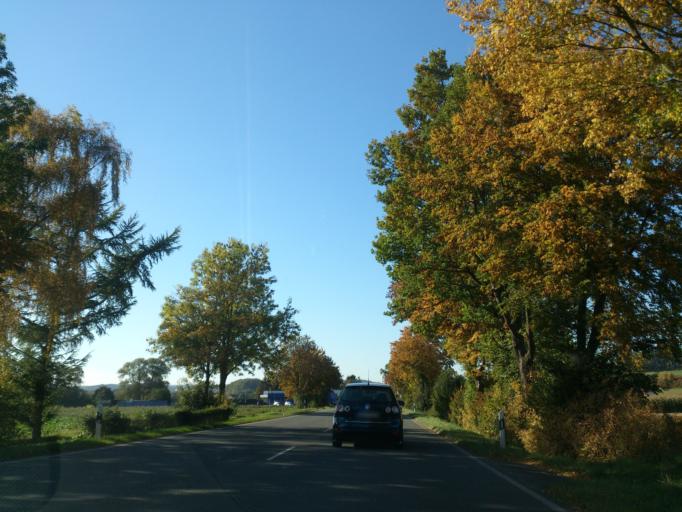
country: DE
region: North Rhine-Westphalia
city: Warburg
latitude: 51.5212
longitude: 9.0626
